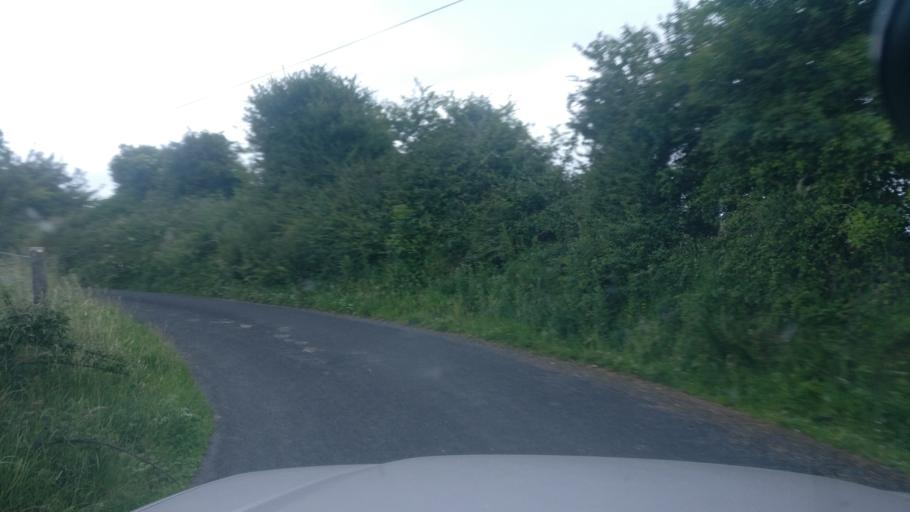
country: IE
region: Connaught
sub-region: County Galway
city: Ballinasloe
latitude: 53.2995
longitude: -8.3657
